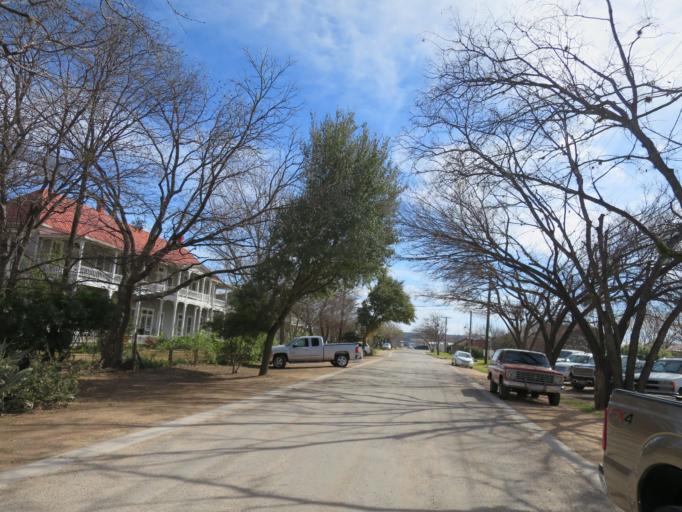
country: US
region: Texas
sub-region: Llano County
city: Kingsland
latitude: 30.6604
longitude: -98.4370
